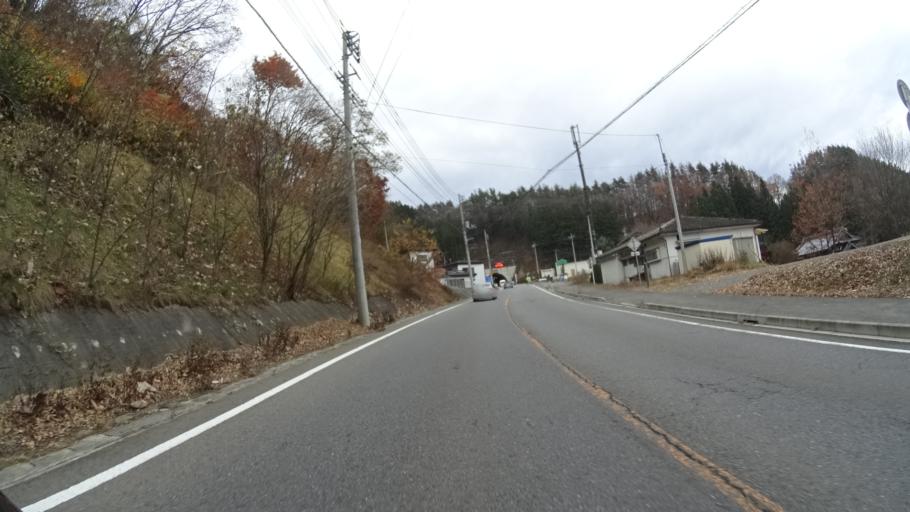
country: JP
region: Gunma
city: Numata
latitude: 36.6609
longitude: 139.1613
